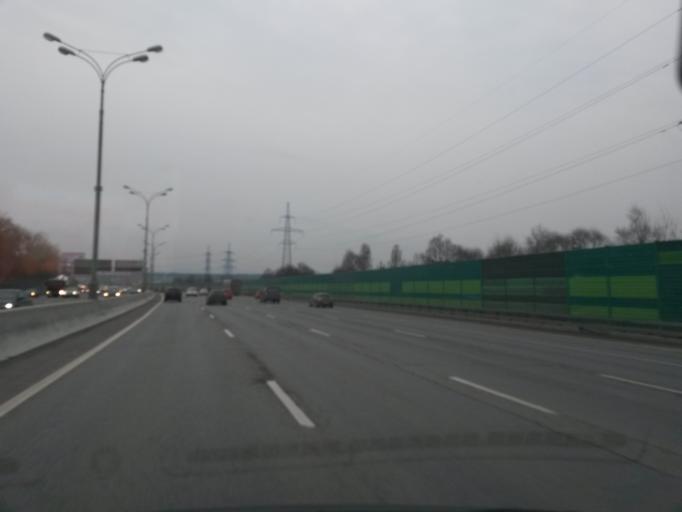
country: RU
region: Moscow
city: Gol'yanovo
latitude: 55.8198
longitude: 37.8381
